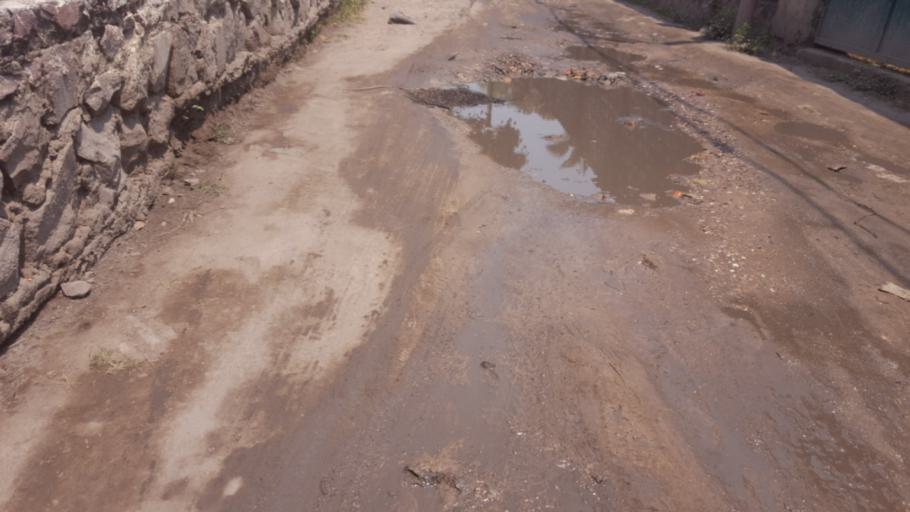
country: CD
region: Kinshasa
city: Kinshasa
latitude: -4.3213
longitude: 15.2884
